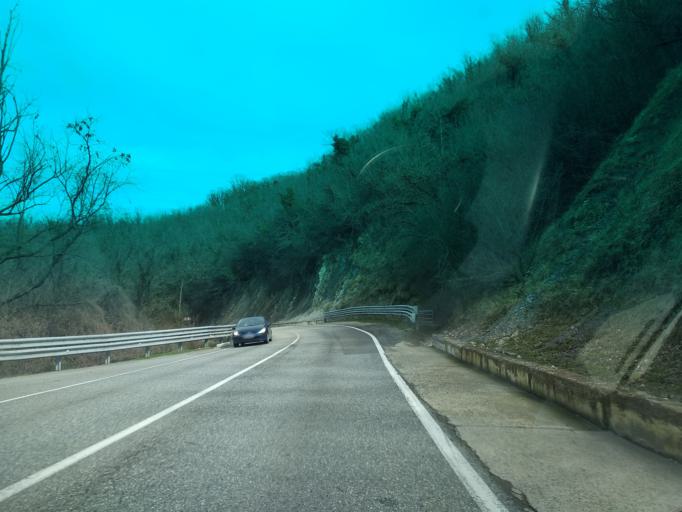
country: RU
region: Krasnodarskiy
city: Shepsi
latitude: 44.0528
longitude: 39.1321
